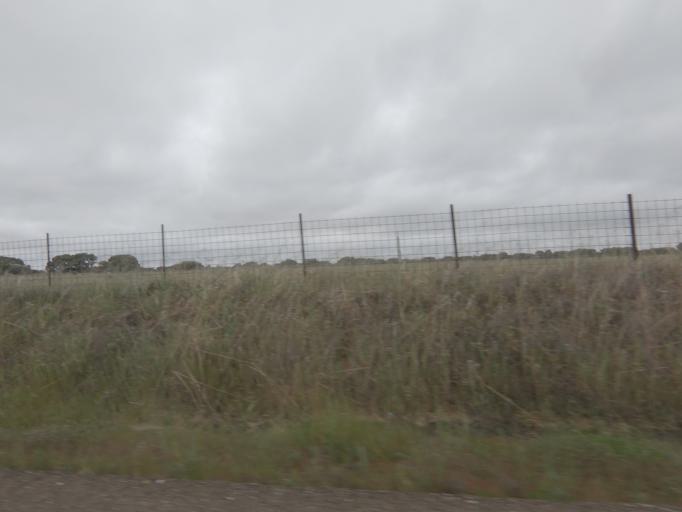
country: ES
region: Extremadura
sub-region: Provincia de Badajoz
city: Villar del Rey
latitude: 39.0294
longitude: -6.8348
